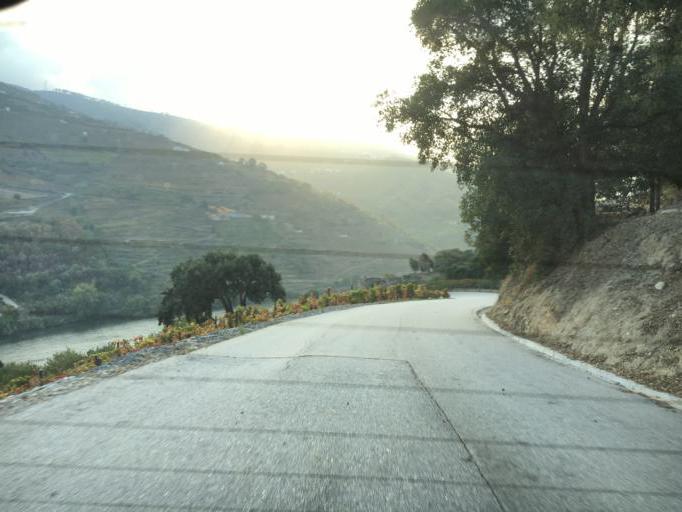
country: PT
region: Vila Real
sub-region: Peso da Regua
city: Godim
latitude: 41.1497
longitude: -7.8166
